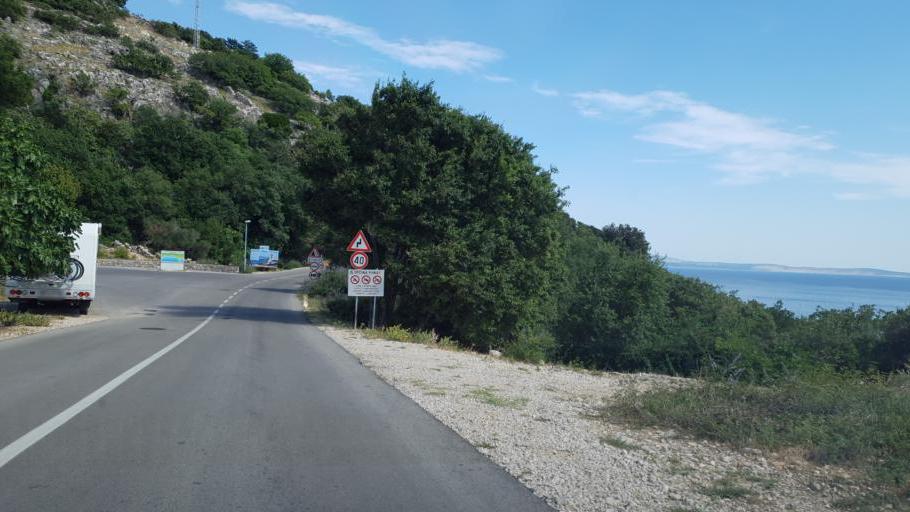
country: HR
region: Primorsko-Goranska
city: Punat
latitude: 44.9657
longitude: 14.6791
